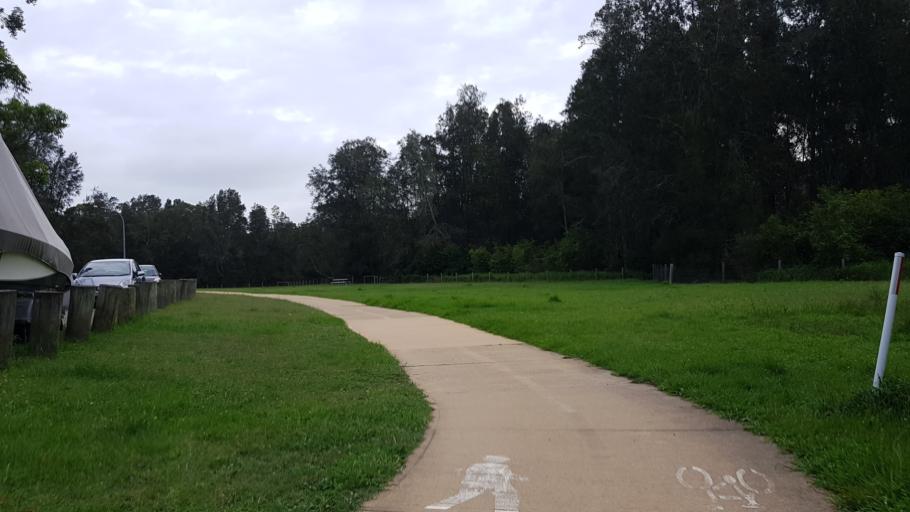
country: AU
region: New South Wales
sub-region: Warringah
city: Narrabeen
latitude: -33.7243
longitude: 151.2760
